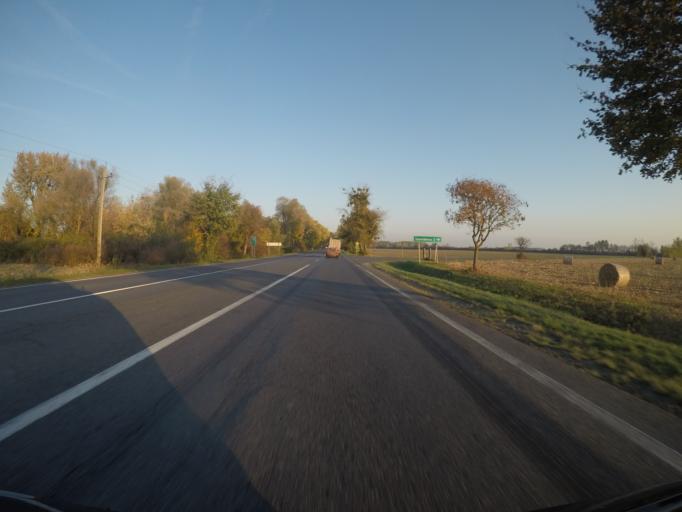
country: HU
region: Baranya
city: Szentlorinc
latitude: 46.0403
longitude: 17.9273
